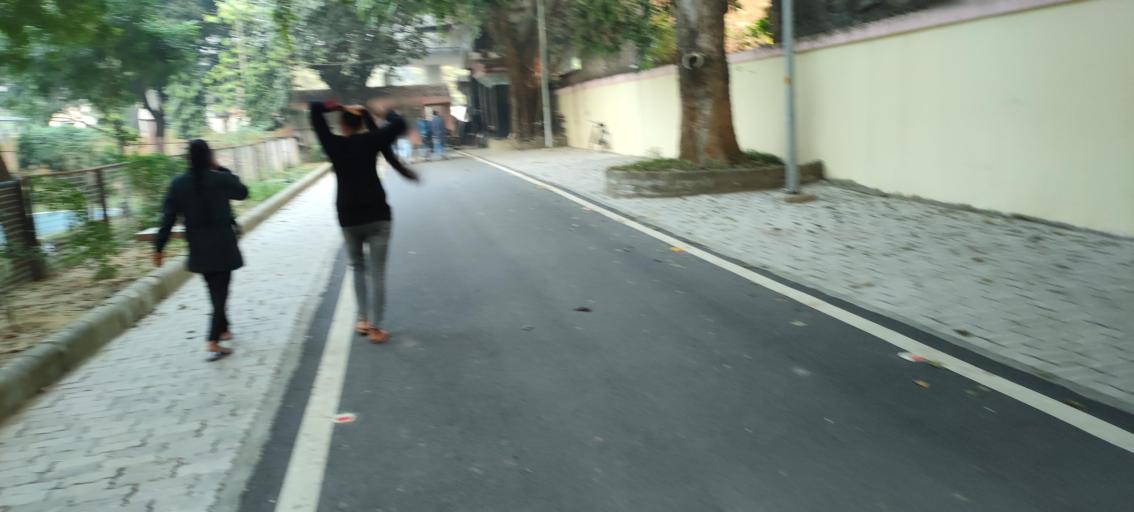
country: IN
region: Uttar Pradesh
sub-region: Allahabad
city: Allahabad
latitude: 25.4914
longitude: 81.8659
